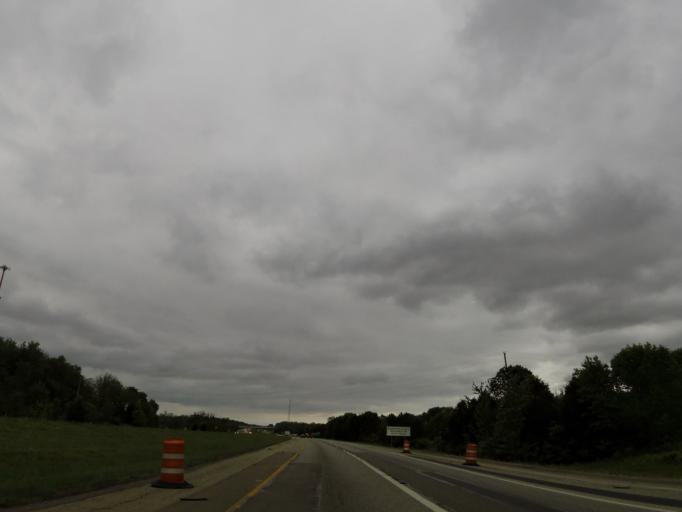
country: US
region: Ohio
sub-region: Warren County
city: Morrow
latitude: 39.4254
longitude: -84.0869
